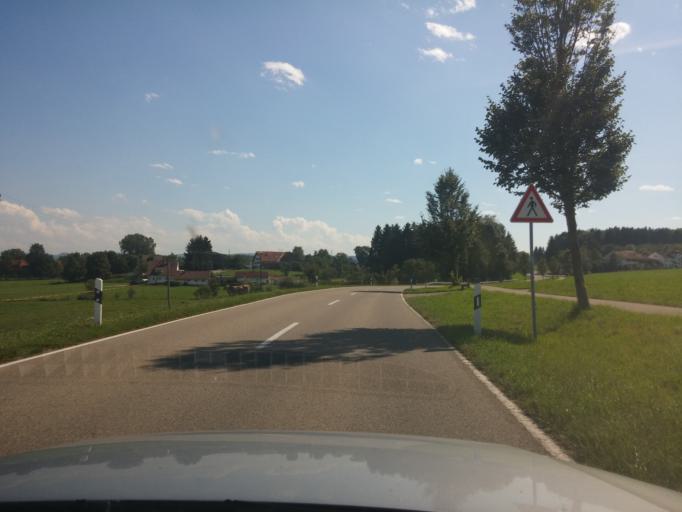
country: DE
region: Bavaria
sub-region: Swabia
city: Legau
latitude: 47.8498
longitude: 10.1248
